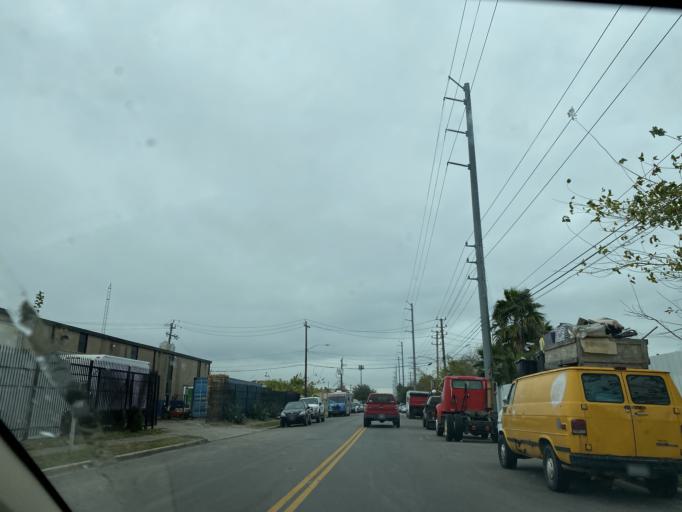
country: US
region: Texas
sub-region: Harris County
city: Piney Point Village
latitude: 29.7270
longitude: -95.5195
